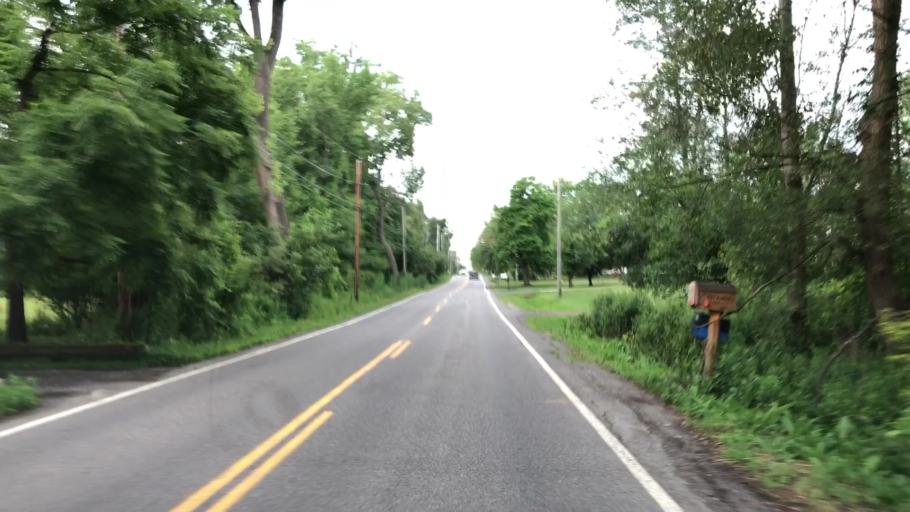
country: US
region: New York
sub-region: Erie County
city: Depew
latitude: 42.8507
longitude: -78.6923
